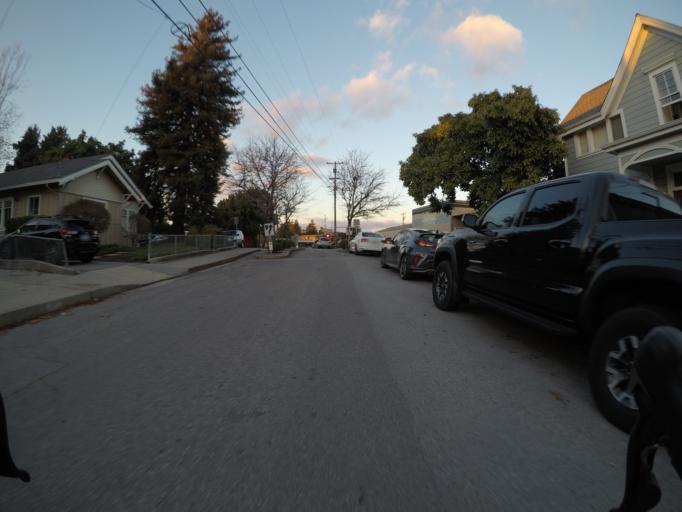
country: US
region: California
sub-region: Santa Cruz County
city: Santa Cruz
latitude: 36.9732
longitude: -122.0215
